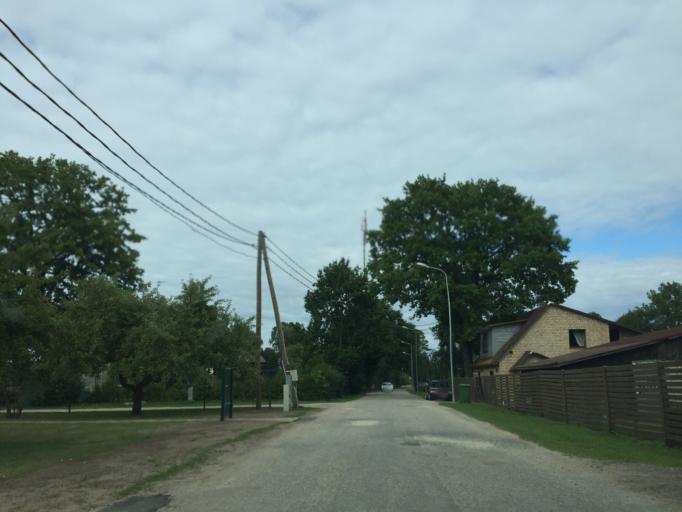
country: LV
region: Riga
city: Jaunciems
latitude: 57.1003
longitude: 24.1911
